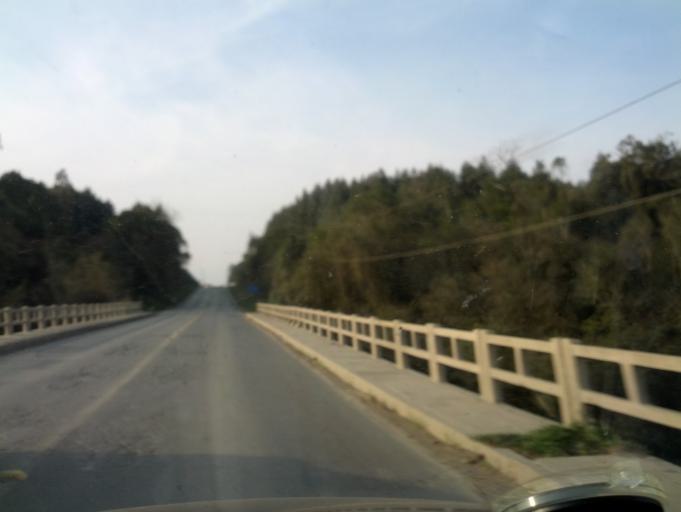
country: BR
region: Santa Catarina
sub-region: Otacilio Costa
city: Otacilio Costa
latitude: -27.5156
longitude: -50.1326
